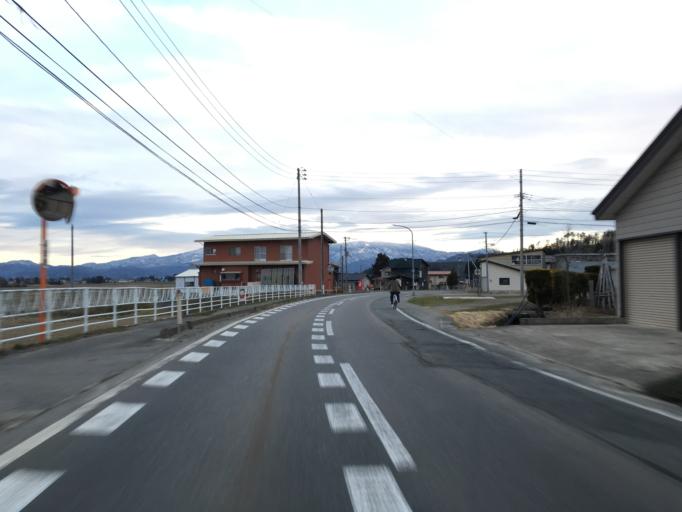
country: JP
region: Yamagata
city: Yonezawa
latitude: 37.9633
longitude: 140.0675
